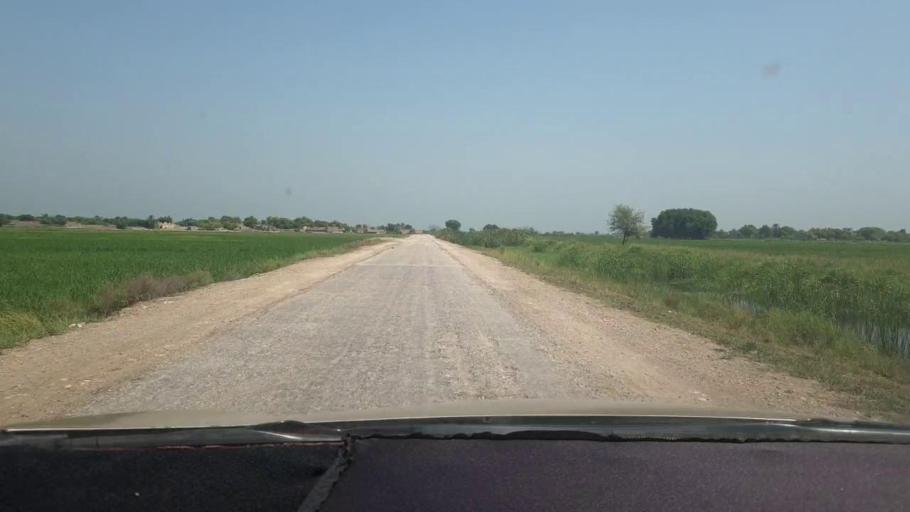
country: PK
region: Sindh
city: Miro Khan
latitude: 27.6863
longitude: 68.0892
